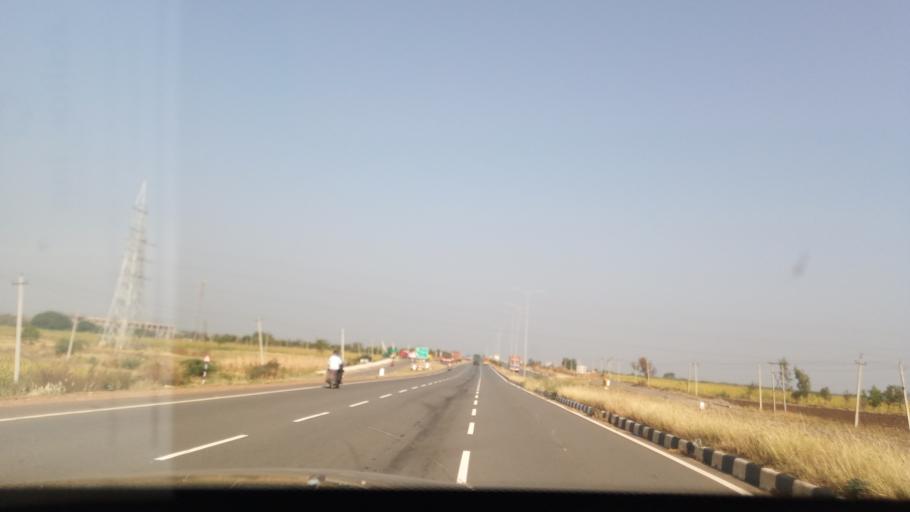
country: IN
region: Karnataka
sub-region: Haveri
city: Haveri
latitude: 14.8325
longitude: 75.3602
